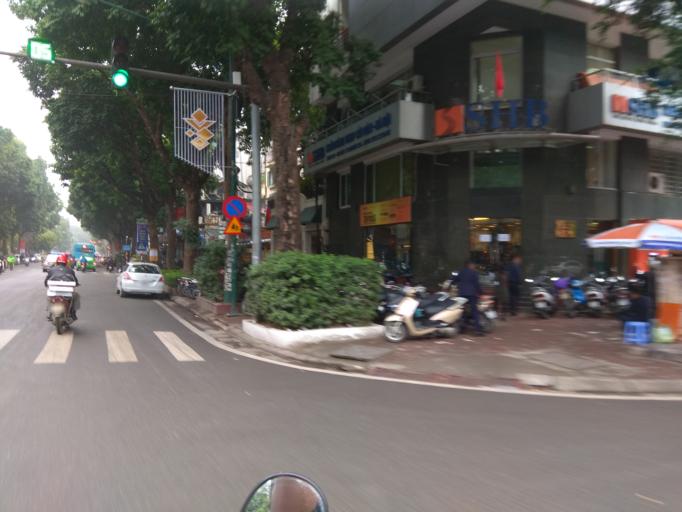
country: VN
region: Ha Noi
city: Hoan Kiem
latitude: 21.0205
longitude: 105.8537
